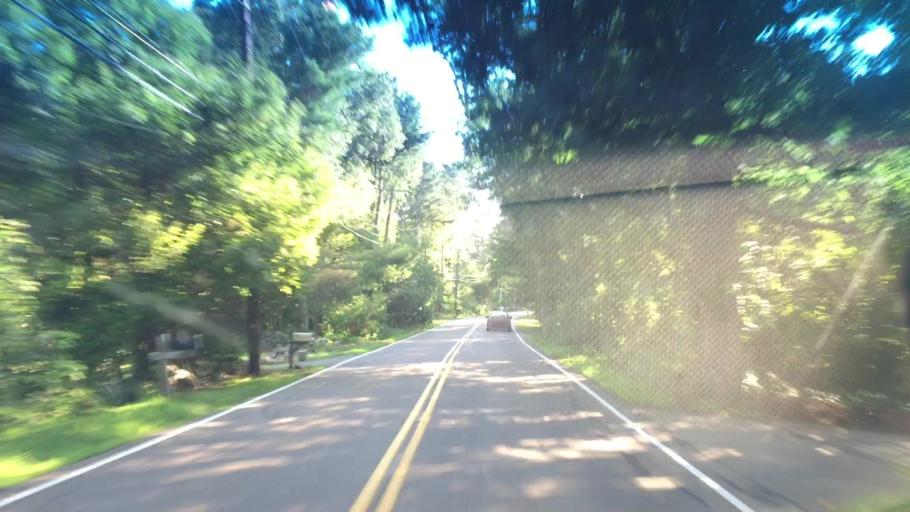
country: US
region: Massachusetts
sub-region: Norfolk County
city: Norfolk
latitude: 42.1315
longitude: -71.2895
